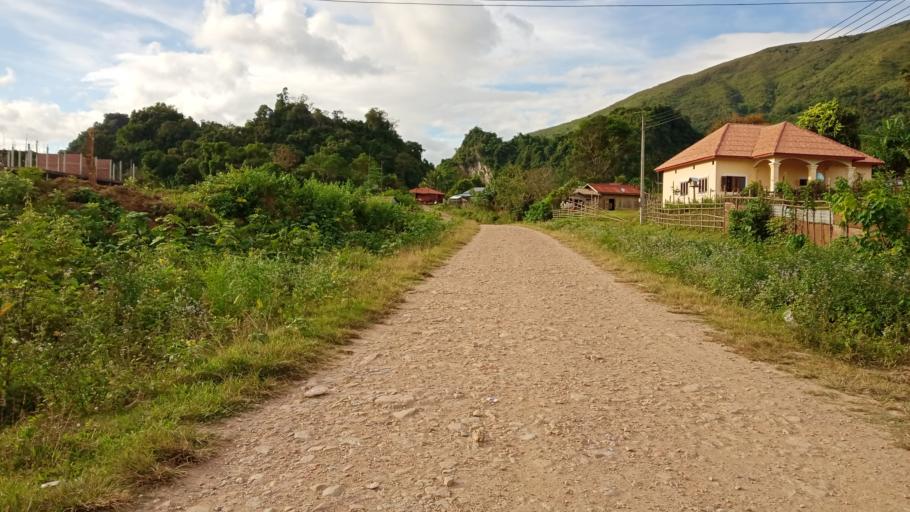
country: LA
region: Xiangkhoang
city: Phonsavan
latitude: 19.1089
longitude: 102.9262
